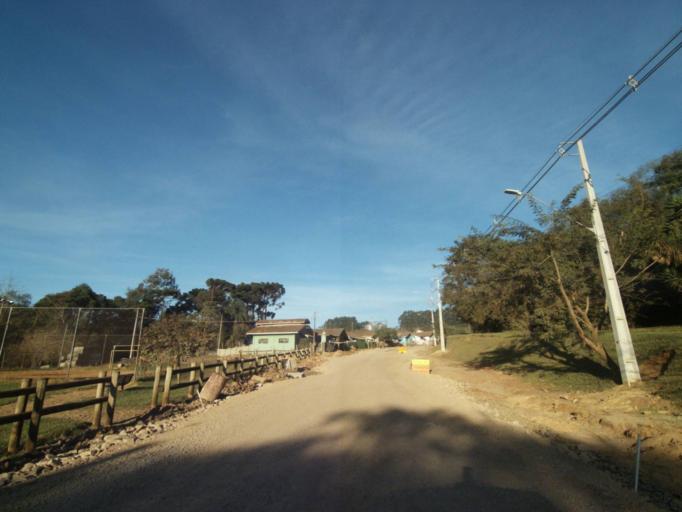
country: BR
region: Parana
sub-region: Tibagi
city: Tibagi
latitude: -24.5197
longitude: -50.4197
